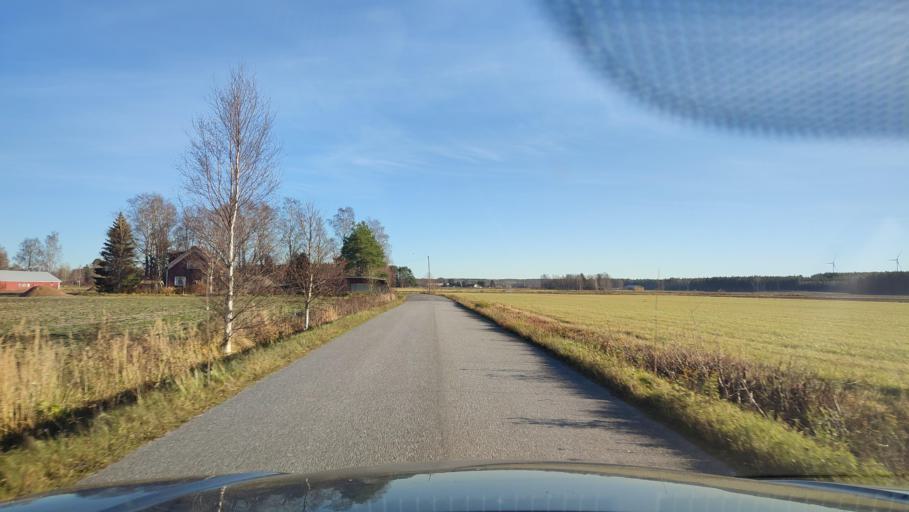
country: FI
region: Southern Ostrobothnia
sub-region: Suupohja
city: Karijoki
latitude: 62.2242
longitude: 21.6400
